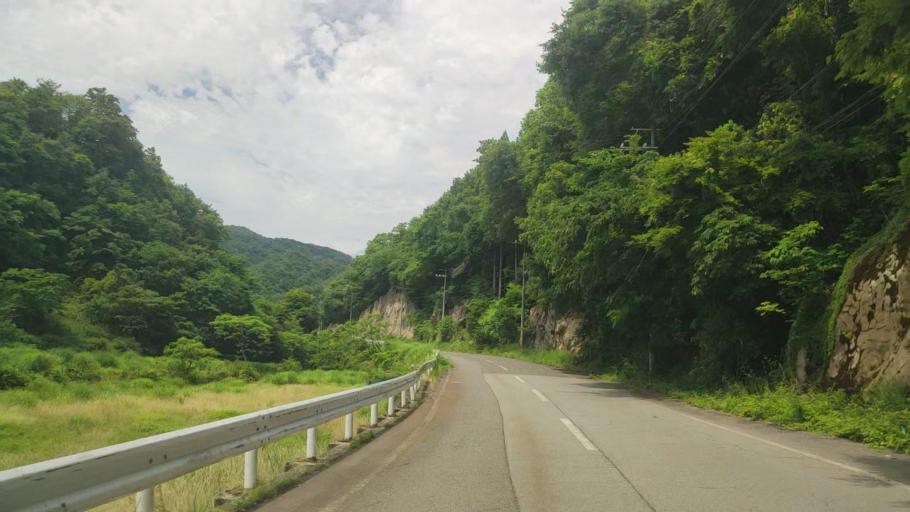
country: JP
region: Hyogo
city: Toyooka
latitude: 35.5245
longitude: 134.7005
